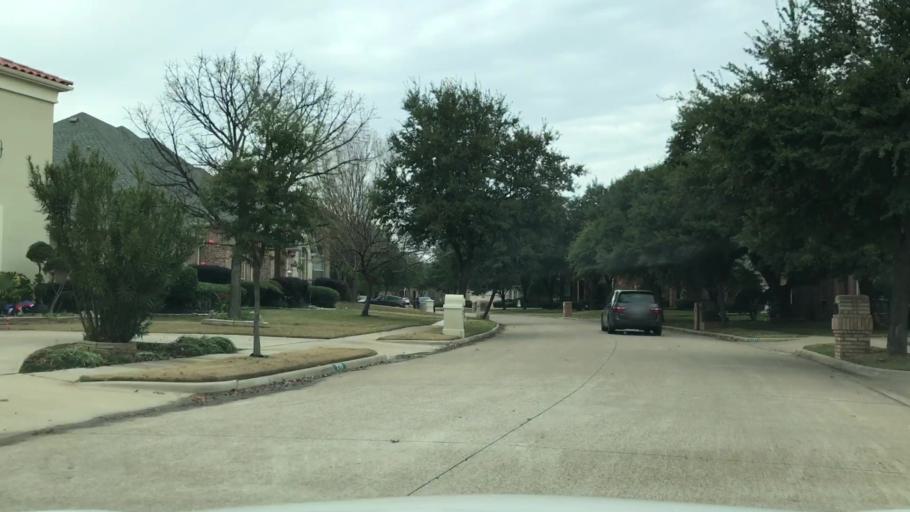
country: US
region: Texas
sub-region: Dallas County
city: Coppell
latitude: 32.9083
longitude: -96.9737
